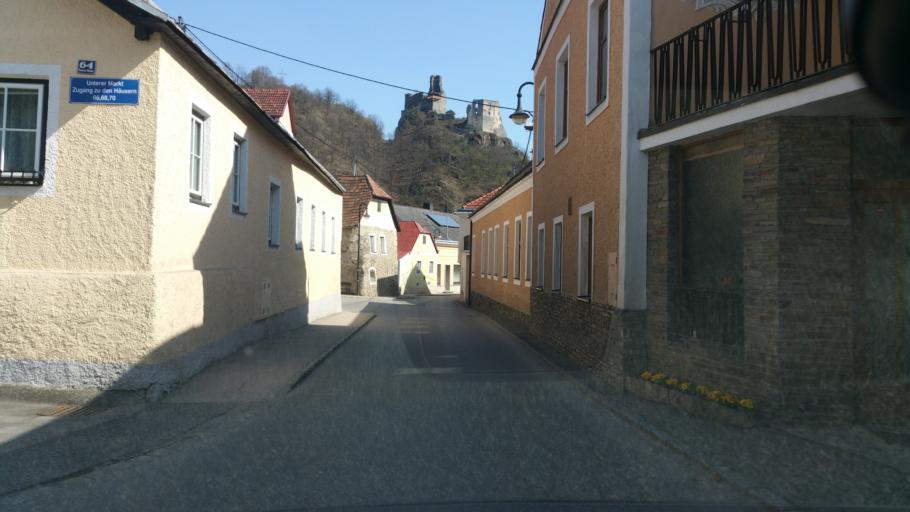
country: AT
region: Lower Austria
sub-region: Politischer Bezirk Krems
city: Senftenberg
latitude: 48.4494
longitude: 15.5600
